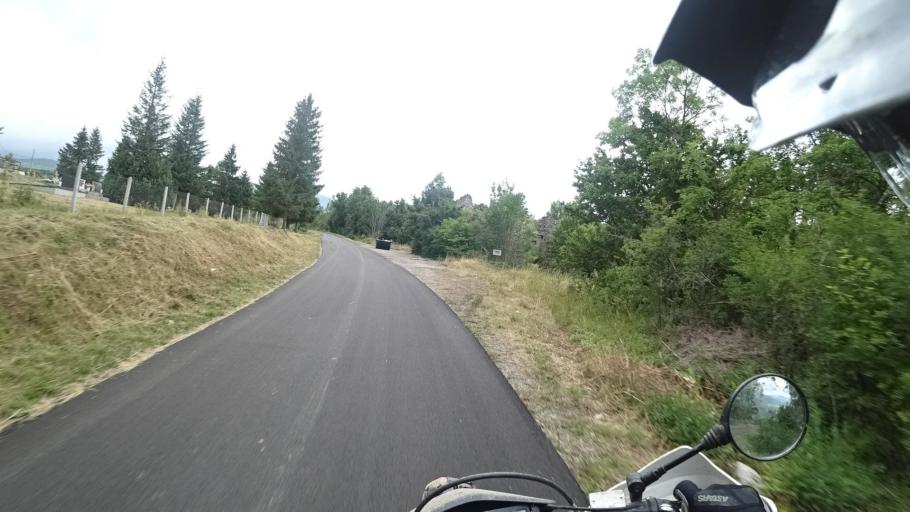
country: HR
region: Zadarska
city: Gracac
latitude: 44.5226
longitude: 15.8073
